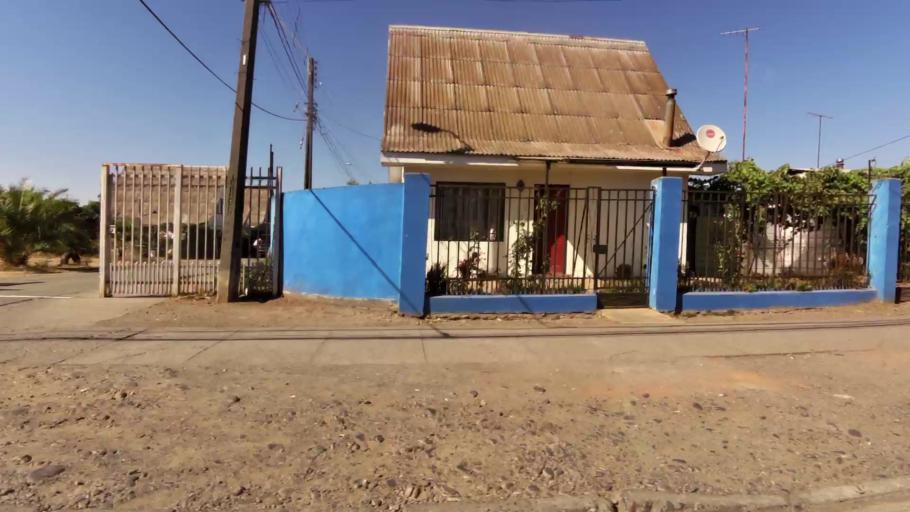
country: CL
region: Maule
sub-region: Provincia de Curico
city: Curico
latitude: -34.9810
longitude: -71.2512
